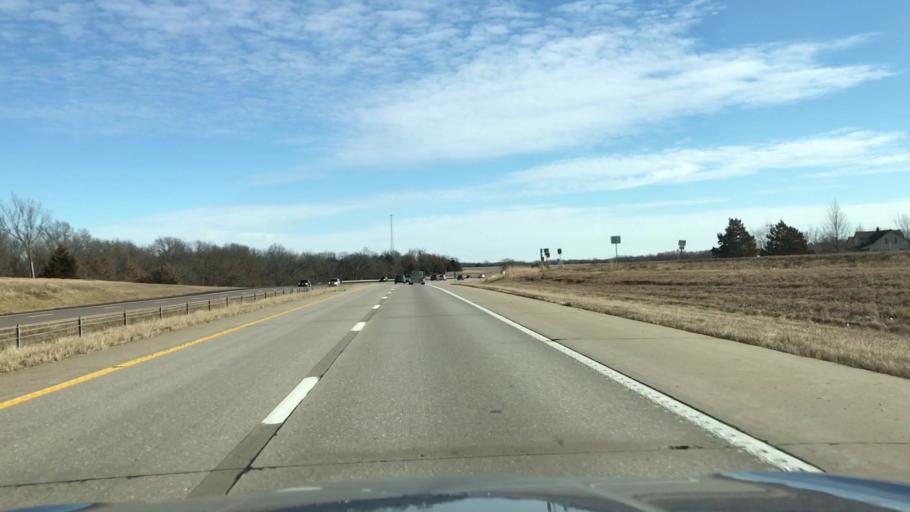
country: US
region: Missouri
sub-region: Montgomery County
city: Montgomery City
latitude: 38.9106
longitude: -91.6623
